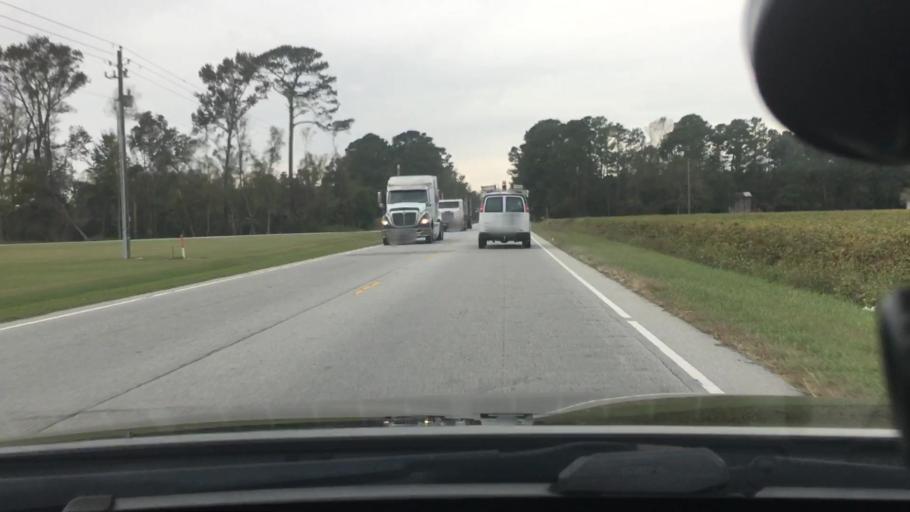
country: US
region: North Carolina
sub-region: Craven County
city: Vanceboro
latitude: 35.2731
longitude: -77.1144
